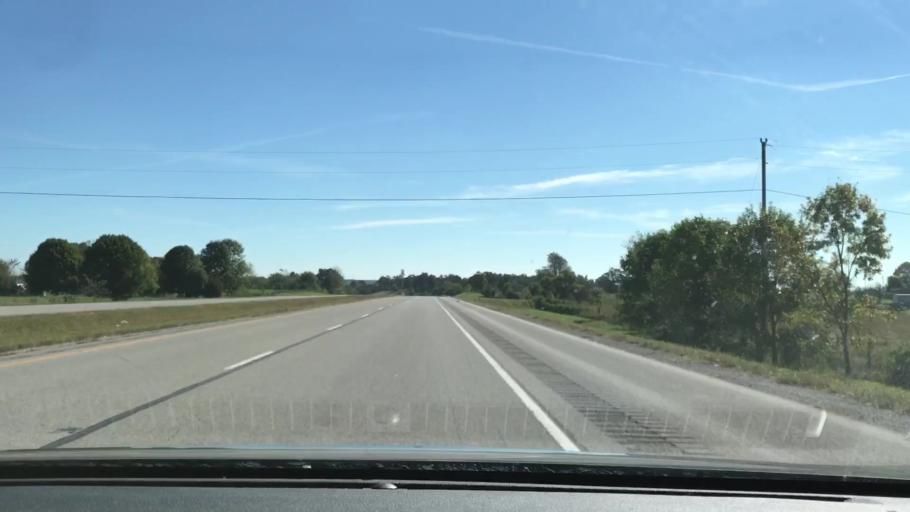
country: US
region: Kentucky
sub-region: Todd County
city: Elkton
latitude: 36.8223
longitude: -87.1974
